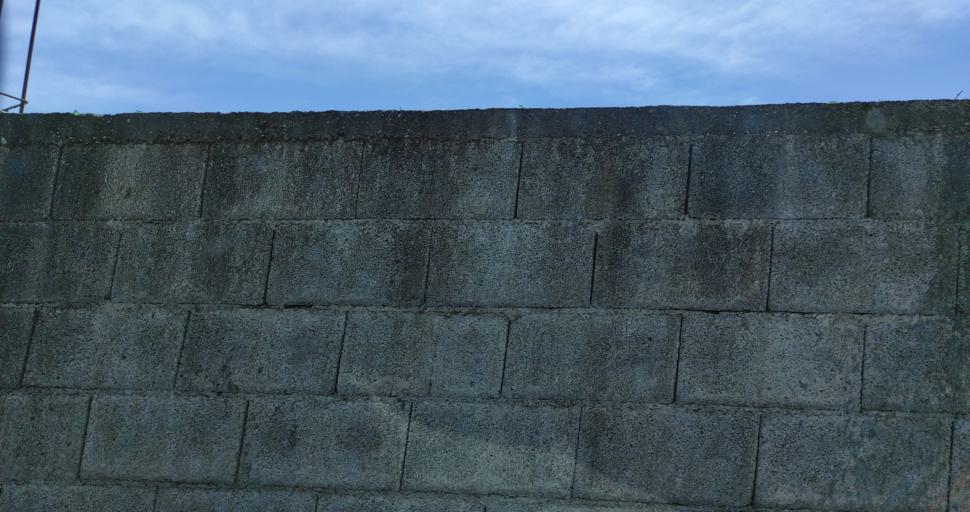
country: AL
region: Shkoder
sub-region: Rrethi i Malesia e Madhe
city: Gruemire
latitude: 42.1389
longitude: 19.5453
